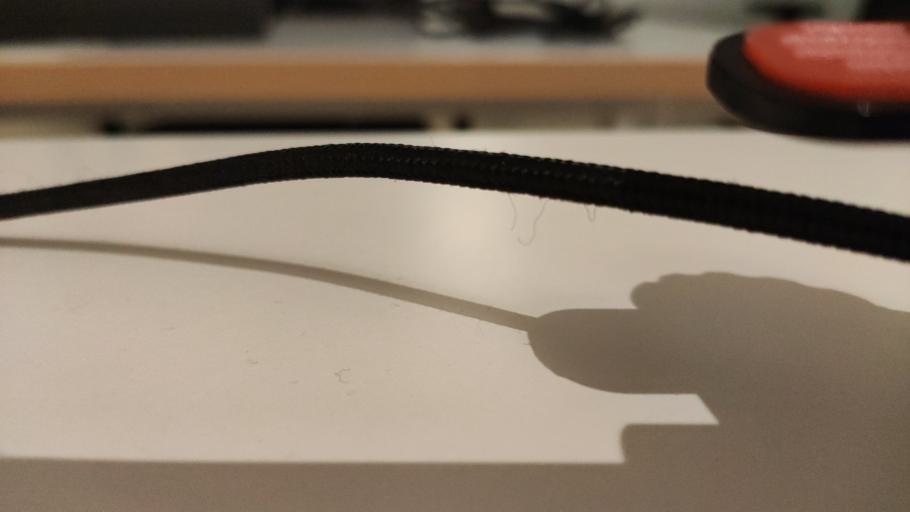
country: RU
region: Moskovskaya
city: Shaburnovo
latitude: 56.4337
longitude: 37.9300
